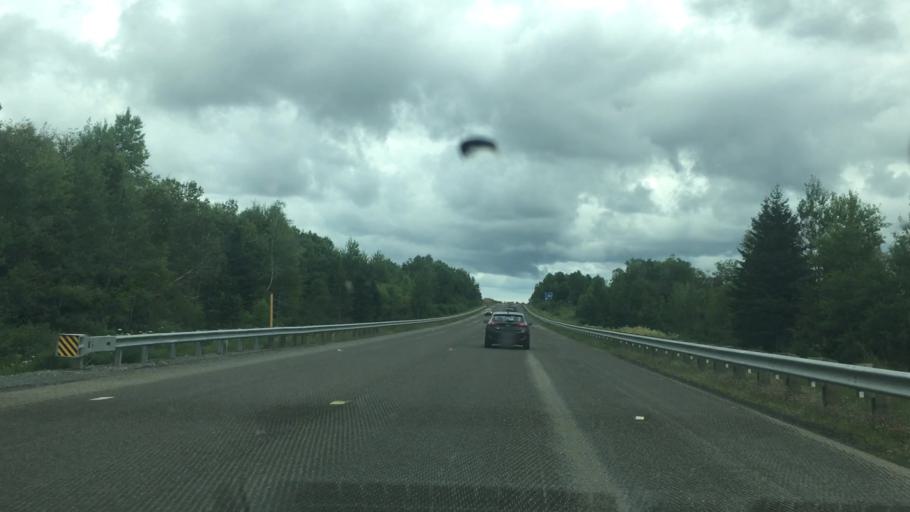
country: CA
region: Nova Scotia
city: Antigonish
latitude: 45.5892
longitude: -62.0736
